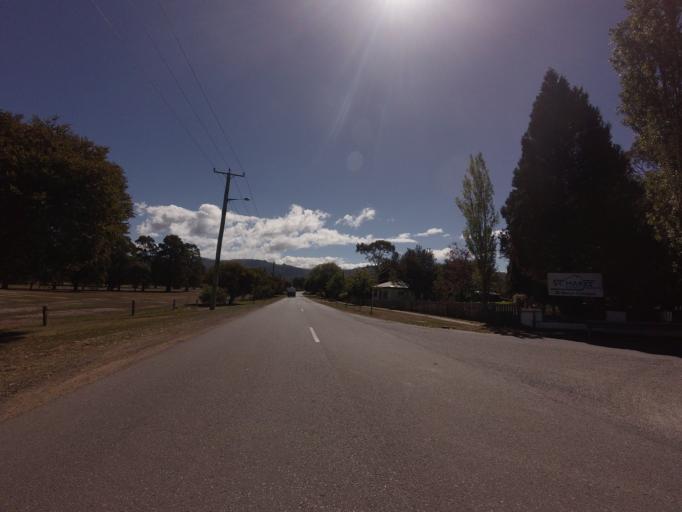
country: AU
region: Tasmania
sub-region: Break O'Day
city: St Helens
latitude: -41.5851
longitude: 148.1872
